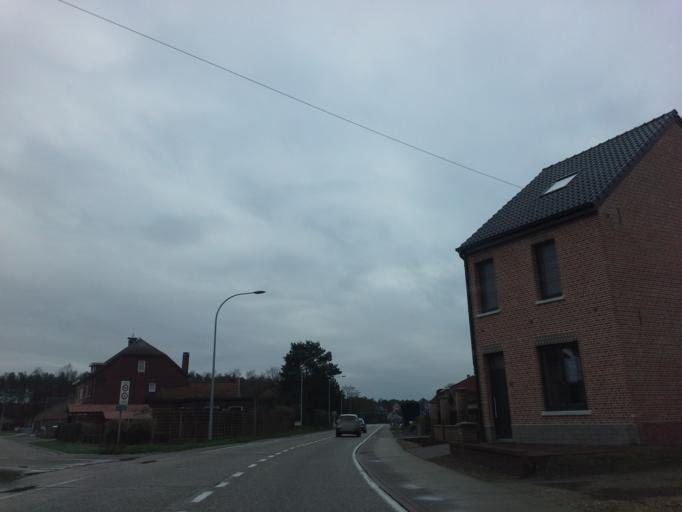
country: BE
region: Flanders
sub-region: Provincie Antwerpen
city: Balen
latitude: 51.1588
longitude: 5.1653
